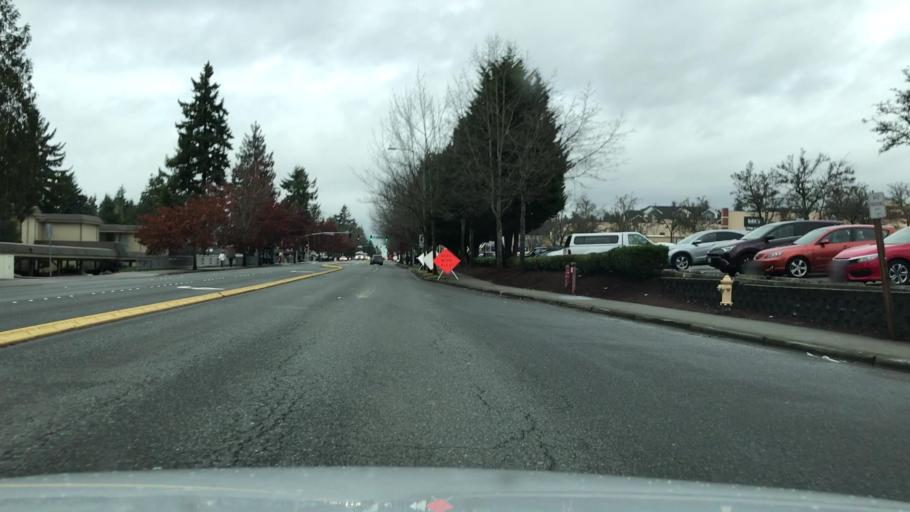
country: US
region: Washington
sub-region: King County
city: Eastgate
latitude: 47.6193
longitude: -122.1323
